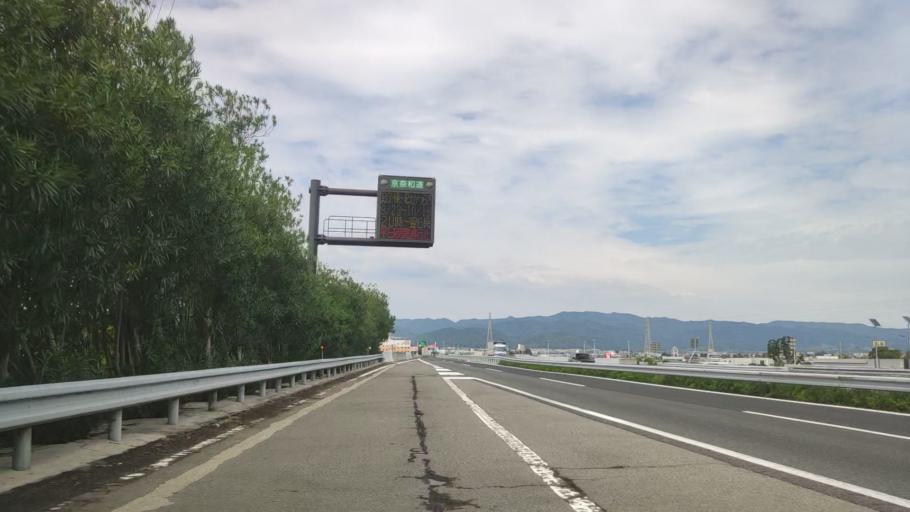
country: JP
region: Wakayama
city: Wakayama-shi
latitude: 34.2324
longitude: 135.2127
